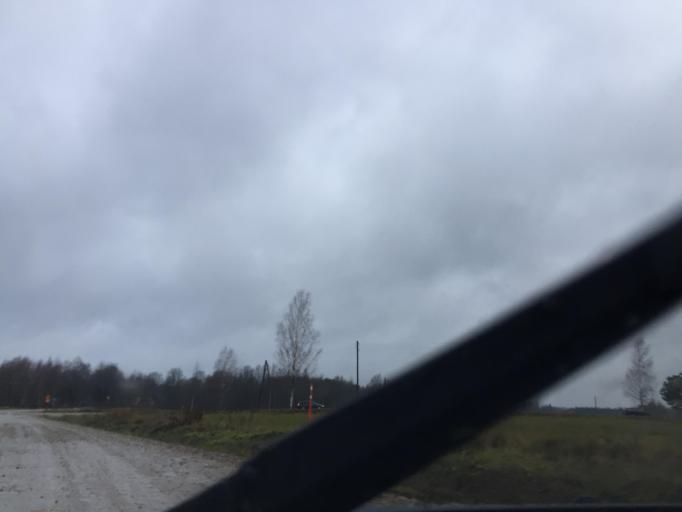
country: LV
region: Salacgrivas
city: Salacgriva
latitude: 57.7736
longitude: 24.5101
